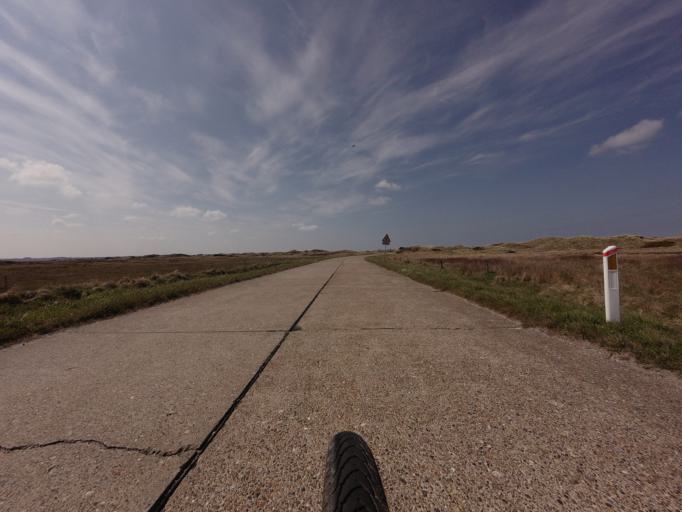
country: DK
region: North Denmark
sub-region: Jammerbugt Kommune
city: Brovst
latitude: 57.1763
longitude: 9.4417
